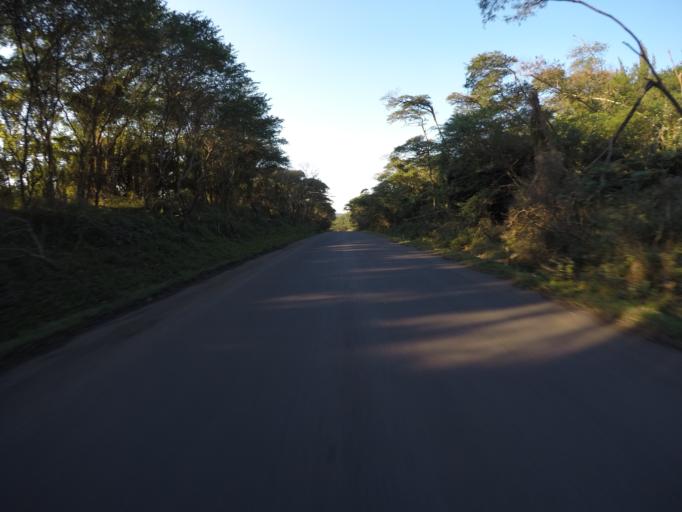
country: ZA
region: KwaZulu-Natal
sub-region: uThungulu District Municipality
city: KwaMbonambi
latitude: -28.6969
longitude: 32.2085
